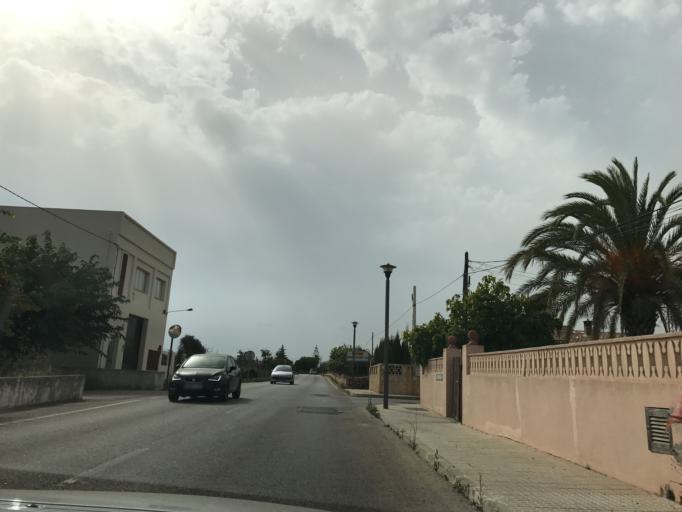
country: ES
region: Balearic Islands
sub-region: Illes Balears
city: Son Servera
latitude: 39.5699
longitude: 3.3688
